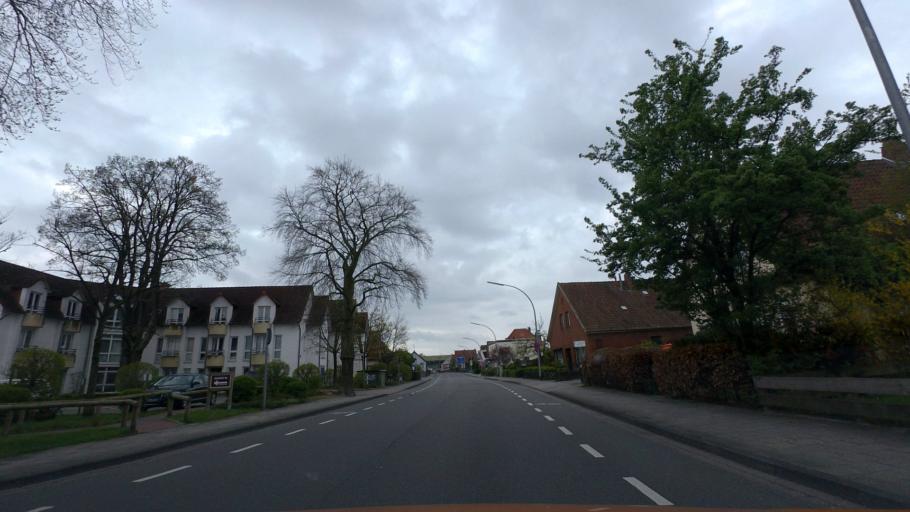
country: DE
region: Lower Saxony
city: Oldenburg
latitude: 53.1256
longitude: 8.2237
